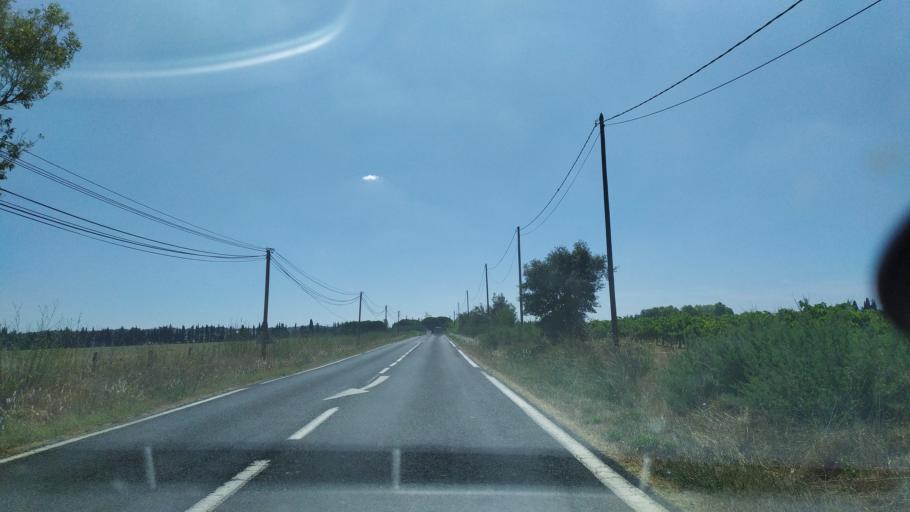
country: FR
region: Languedoc-Roussillon
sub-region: Departement du Gard
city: Vauvert
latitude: 43.7162
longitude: 4.2645
